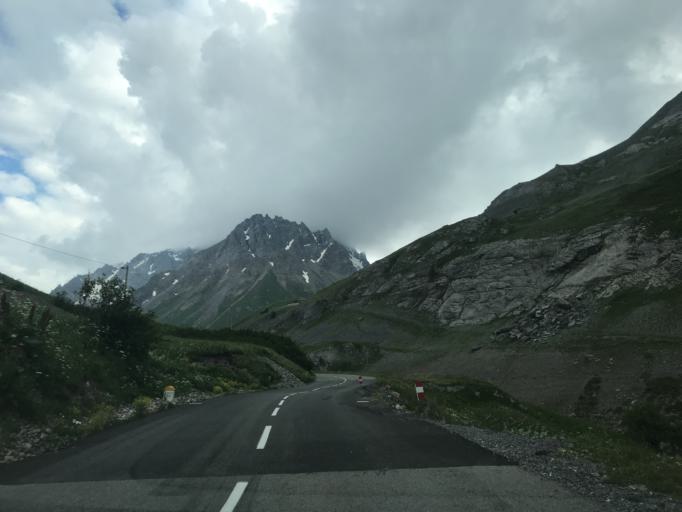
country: FR
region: Rhone-Alpes
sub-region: Departement de la Savoie
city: Valloire
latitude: 45.0958
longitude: 6.4304
